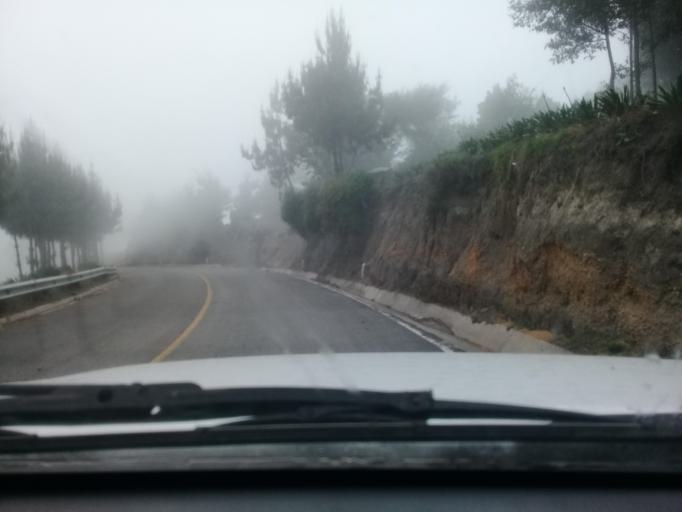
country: MX
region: Veracruz
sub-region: Mariano Escobedo
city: Texmola
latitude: 18.9580
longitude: -97.2210
